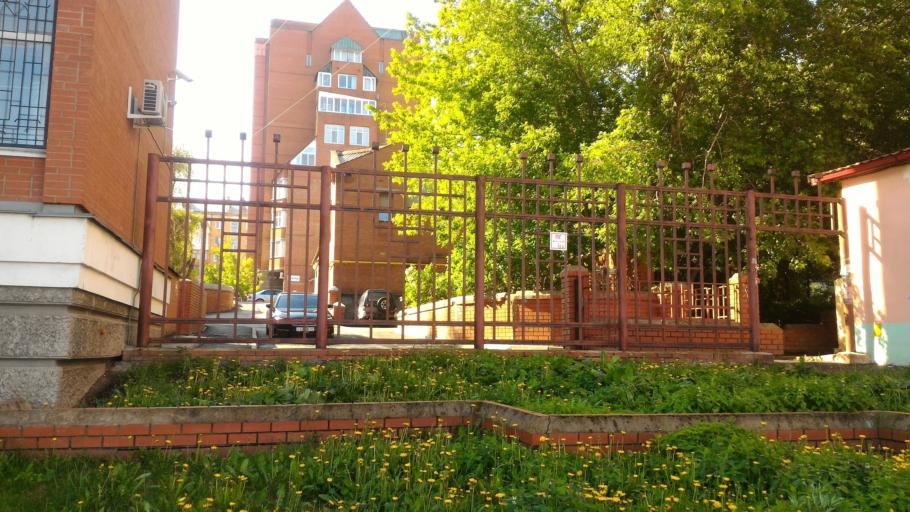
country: RU
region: Perm
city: Perm
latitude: 58.0177
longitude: 56.2485
